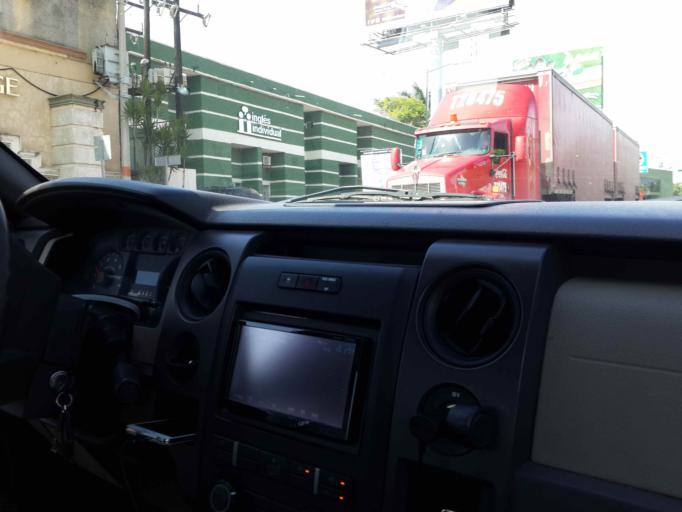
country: MX
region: Tamaulipas
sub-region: Tampico
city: Tampico
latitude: 22.2495
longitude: -97.8671
